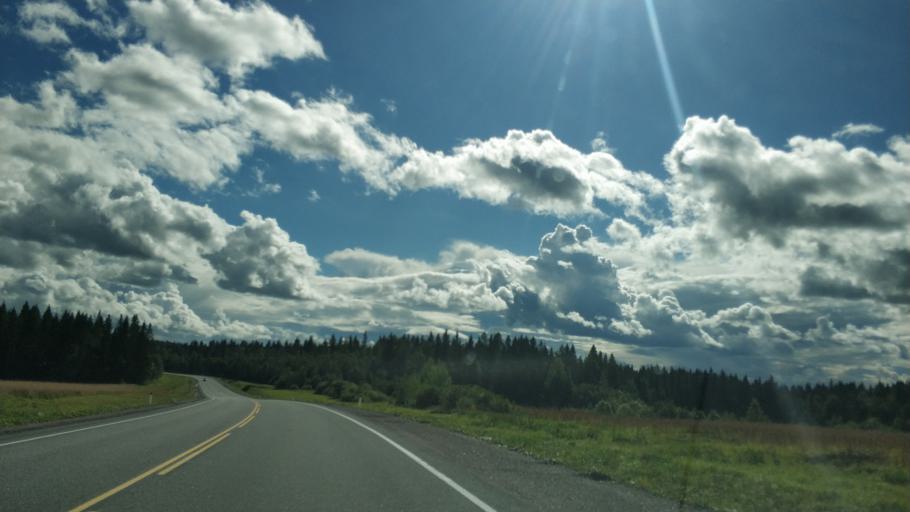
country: RU
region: Republic of Karelia
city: Ruskeala
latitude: 61.8820
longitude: 30.6434
